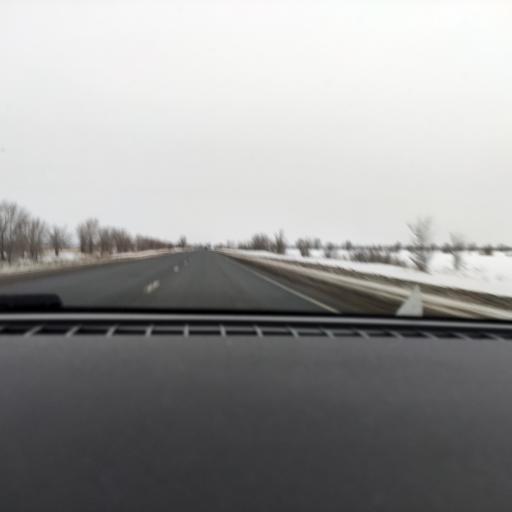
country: RU
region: Samara
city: Kinel'
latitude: 53.1650
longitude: 50.5143
